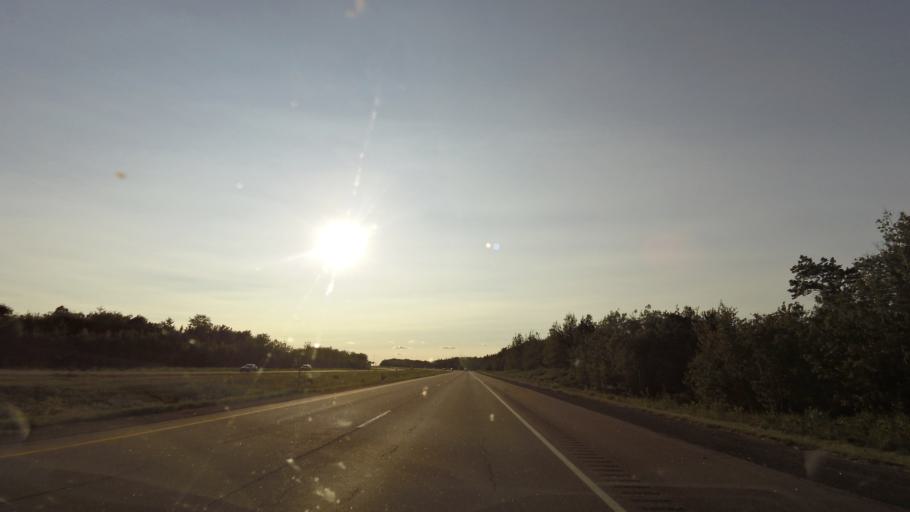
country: CA
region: New Brunswick
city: Dieppe
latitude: 46.1298
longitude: -64.6575
